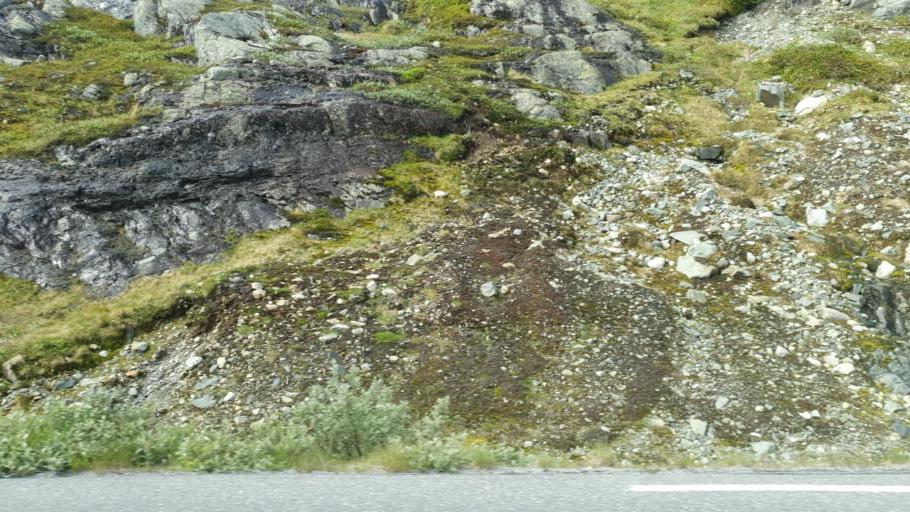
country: NO
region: Oppland
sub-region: Vestre Slidre
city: Slidre
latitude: 61.3403
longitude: 8.8140
